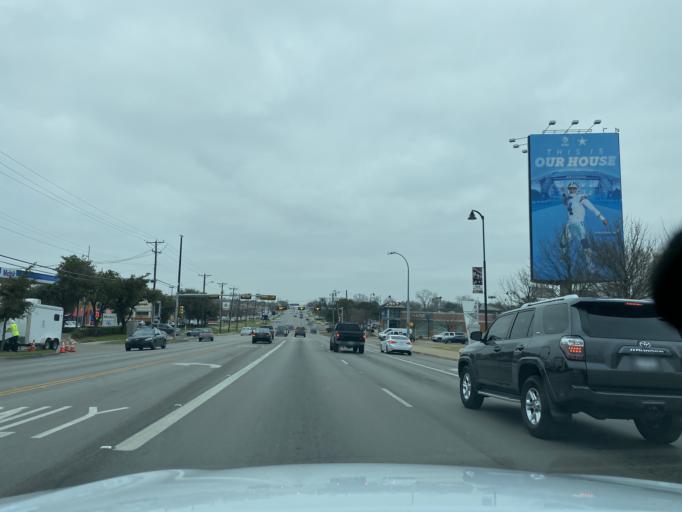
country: US
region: Texas
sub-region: Tarrant County
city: Arlington
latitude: 32.7491
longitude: -97.0973
